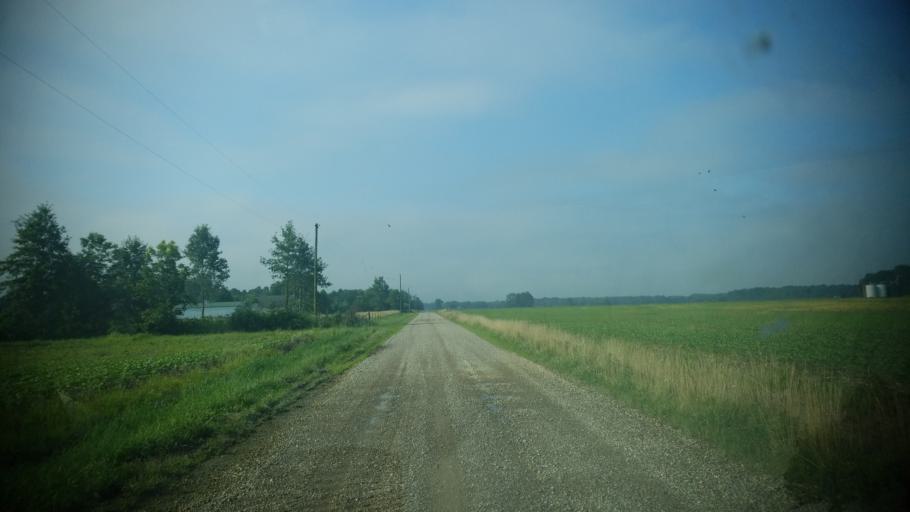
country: US
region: Illinois
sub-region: Clay County
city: Flora
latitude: 38.5977
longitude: -88.3643
